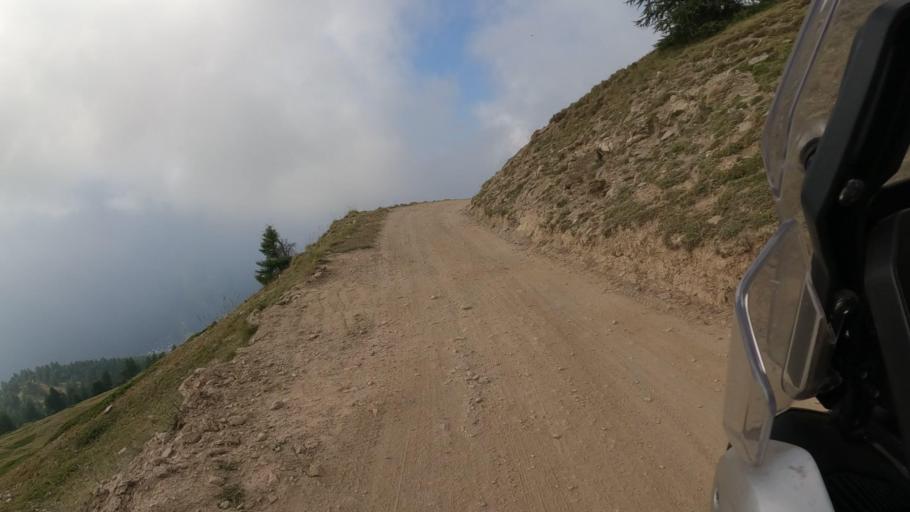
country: IT
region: Piedmont
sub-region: Provincia di Torino
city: Pragelato-Rua
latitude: 45.0333
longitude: 6.9261
